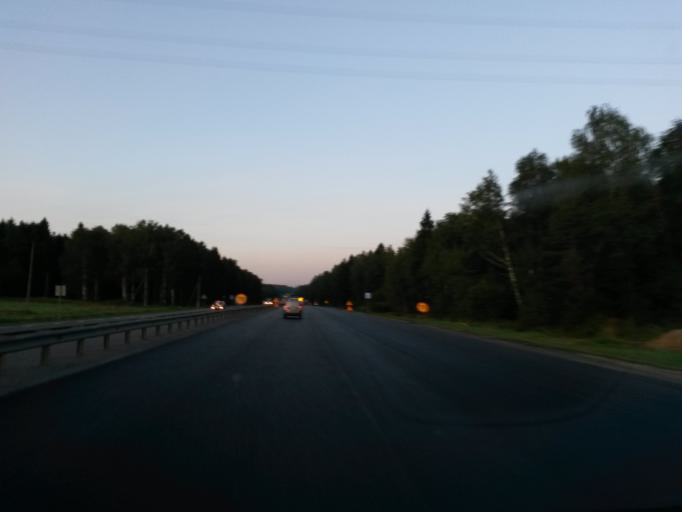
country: RU
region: Moskovskaya
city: Svatkovo
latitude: 56.3200
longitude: 38.2491
